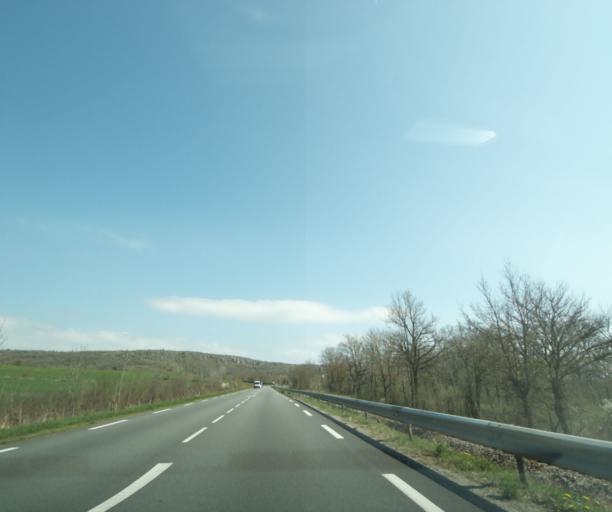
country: FR
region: Midi-Pyrenees
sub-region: Departement de l'Aveyron
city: La Loubiere
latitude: 44.3882
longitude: 2.6734
